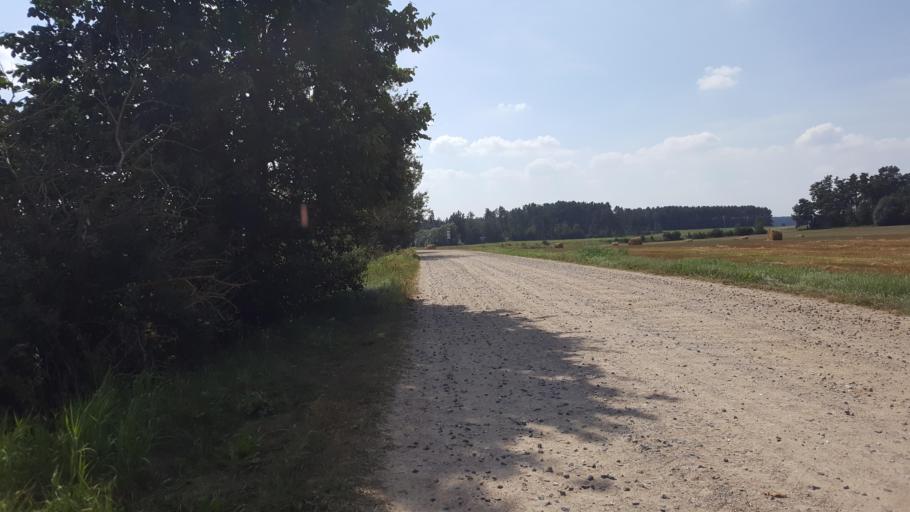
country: PL
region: Podlasie
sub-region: Powiat hajnowski
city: Czeremcha
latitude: 52.5463
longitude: 23.5458
